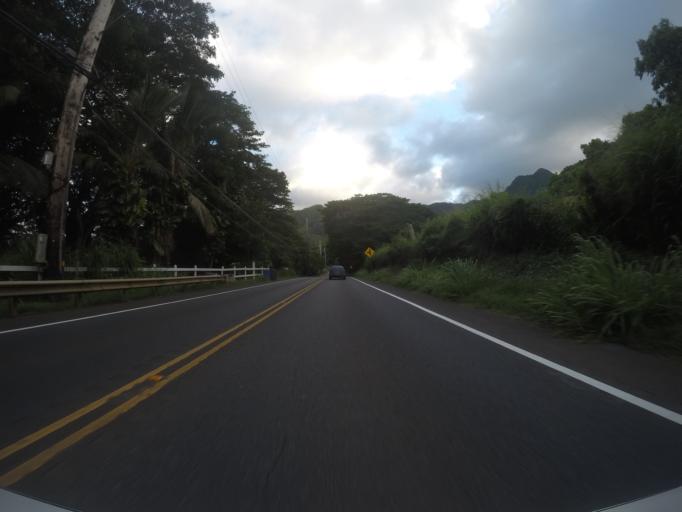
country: US
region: Hawaii
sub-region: Honolulu County
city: Ka'a'awa
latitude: 21.5109
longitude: -157.8523
